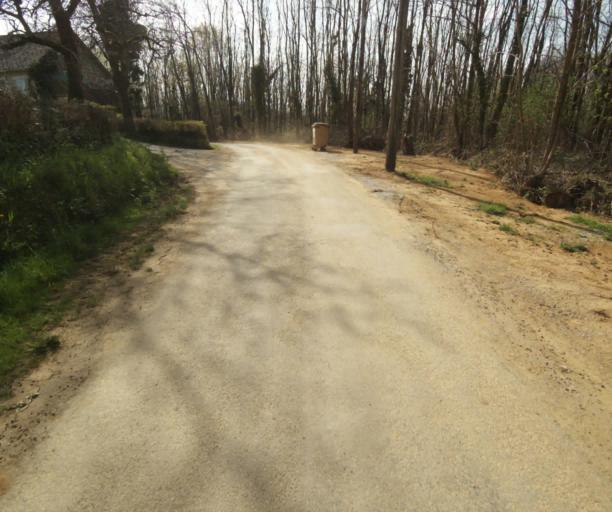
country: FR
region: Limousin
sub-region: Departement de la Correze
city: Seilhac
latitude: 45.3442
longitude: 1.7384
